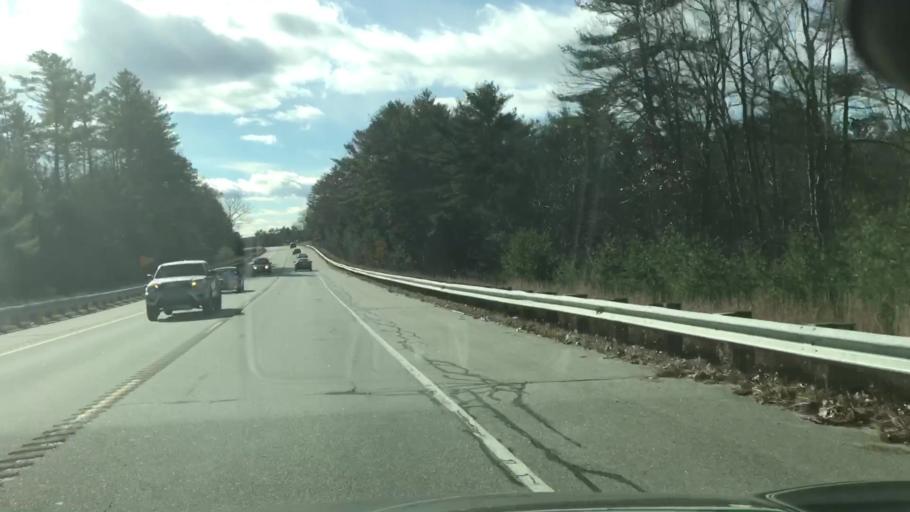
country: US
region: New Hampshire
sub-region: Merrimack County
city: Pittsfield
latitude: 43.2890
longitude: -71.3574
